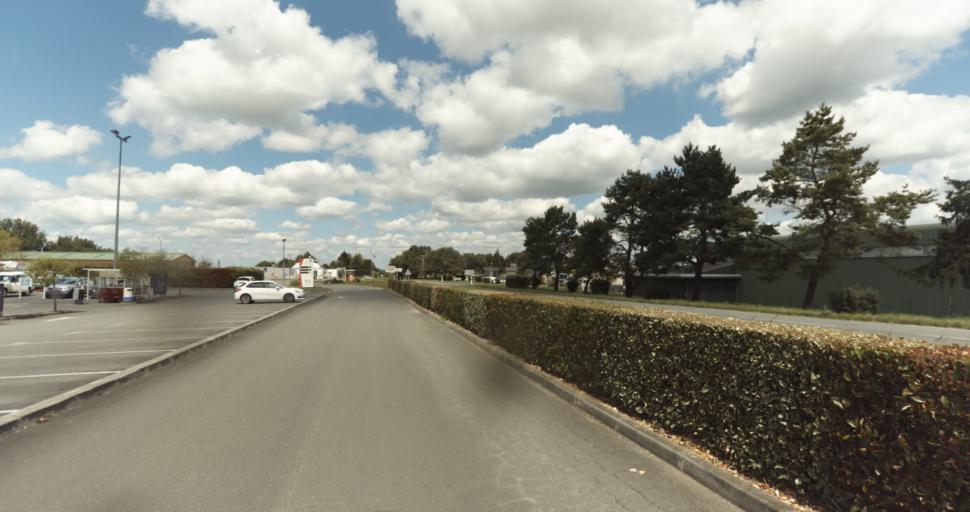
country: FR
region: Aquitaine
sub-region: Departement de la Dordogne
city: Beaumont-du-Perigord
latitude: 44.7536
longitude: 0.7733
